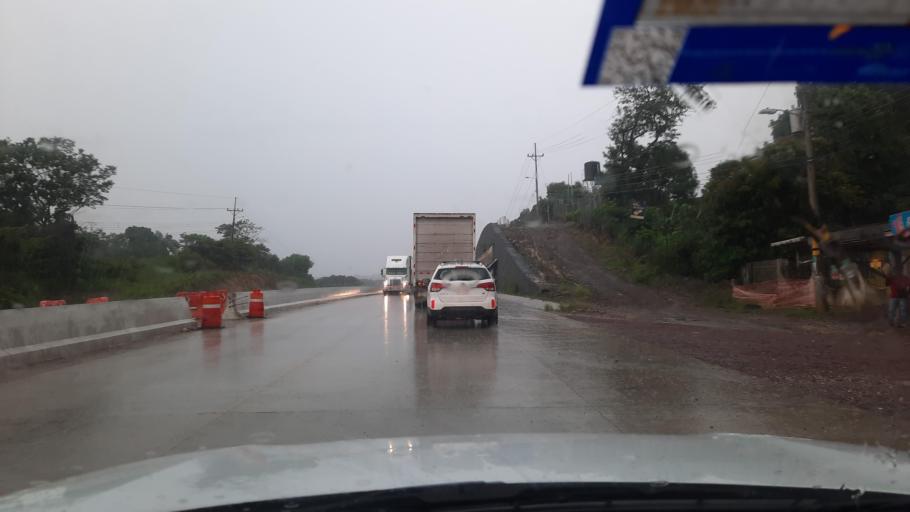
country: CR
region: Guanacaste
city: Juntas
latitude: 10.3141
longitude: -85.0451
